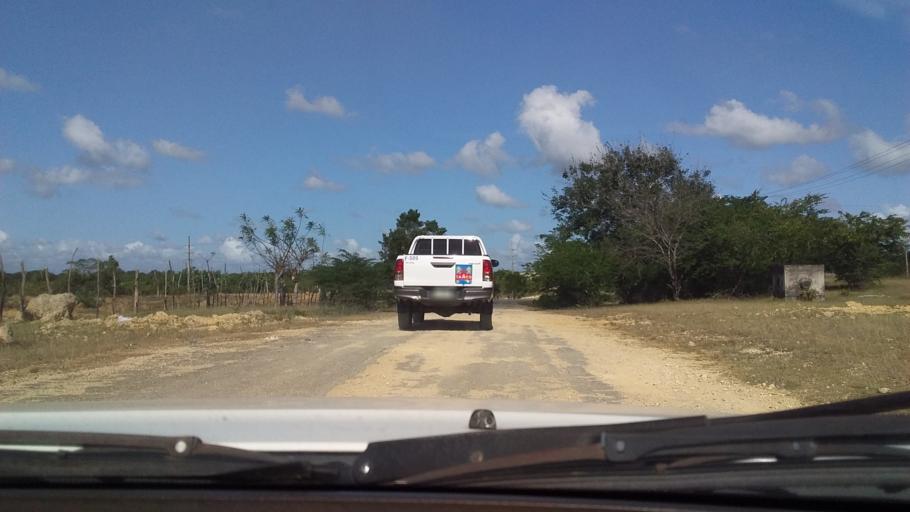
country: DO
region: Santo Domingo
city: Guerra
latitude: 18.5688
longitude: -69.7843
